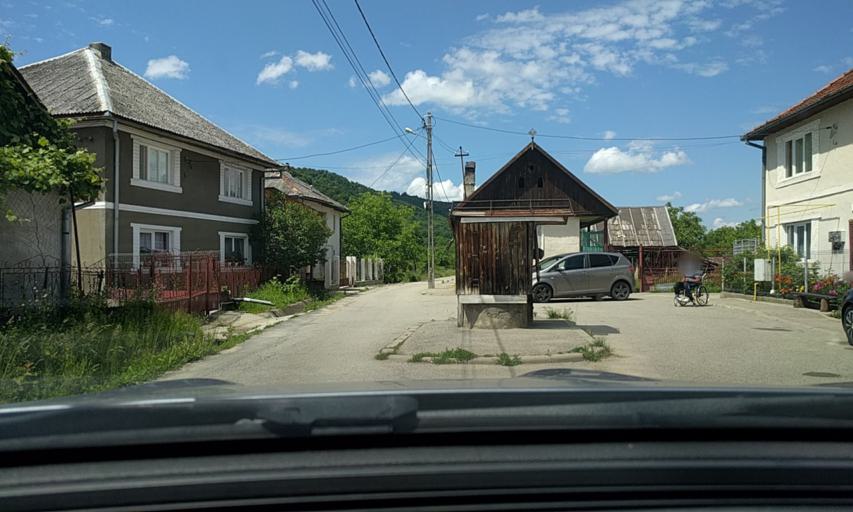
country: RO
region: Bistrita-Nasaud
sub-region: Oras Nasaud
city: Nasaud
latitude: 47.2795
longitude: 24.4035
